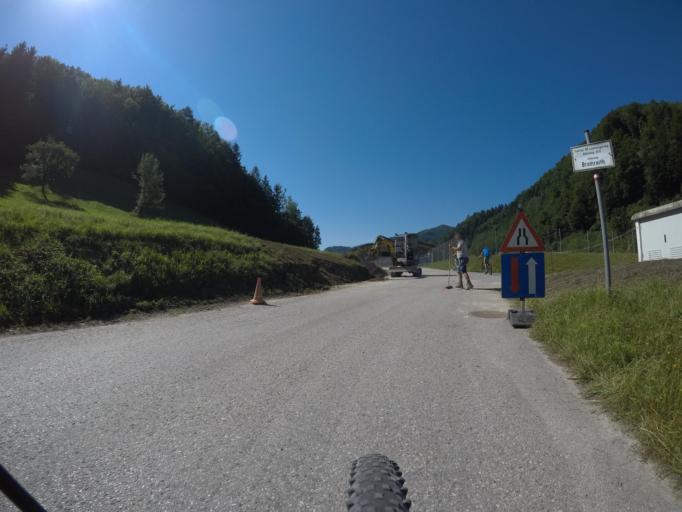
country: AT
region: Lower Austria
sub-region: Waidhofen an der Ybbs Stadt
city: Waidhofen an der Ybbs
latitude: 47.9423
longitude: 14.8244
